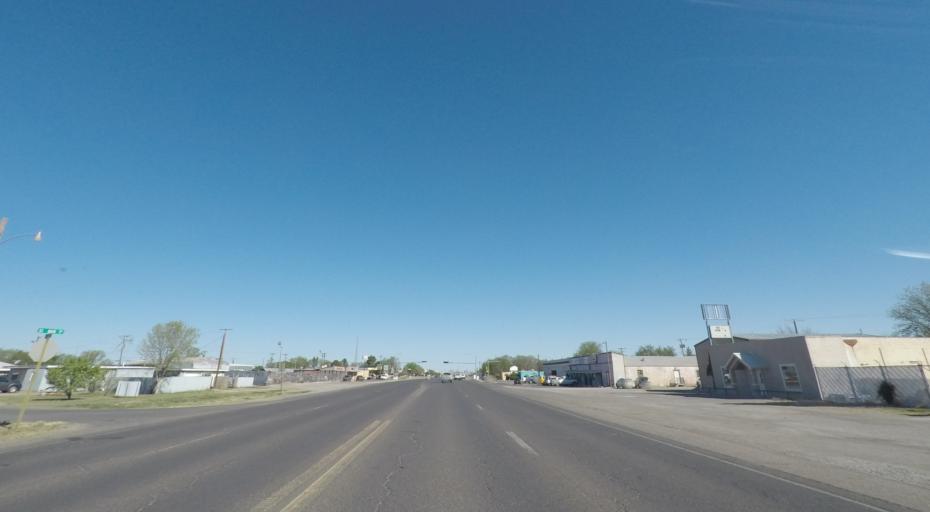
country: US
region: New Mexico
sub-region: Chaves County
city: Roswell
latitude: 33.3711
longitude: -104.5169
